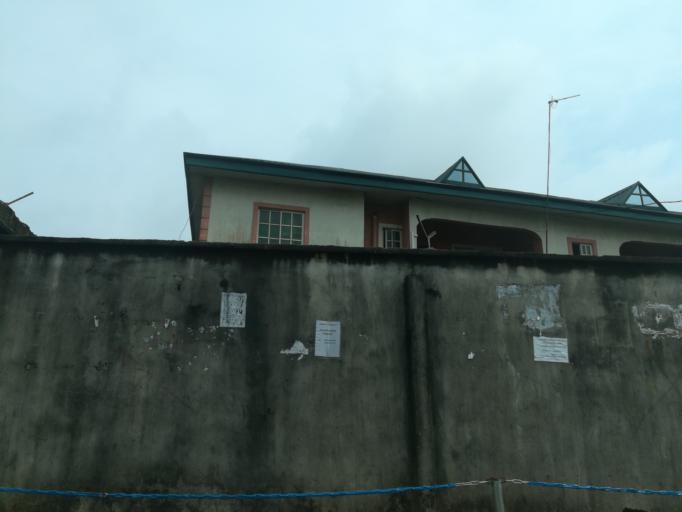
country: NG
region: Rivers
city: Port Harcourt
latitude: 4.8805
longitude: 6.9753
